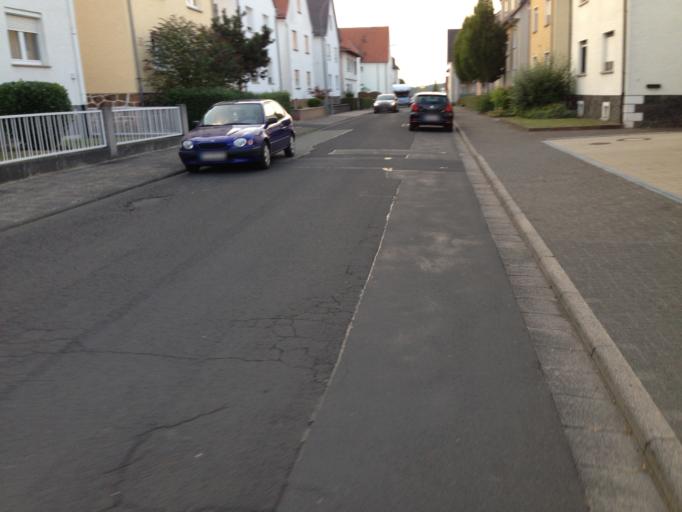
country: DE
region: Hesse
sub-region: Regierungsbezirk Giessen
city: Langgons
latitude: 50.5295
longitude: 8.6595
